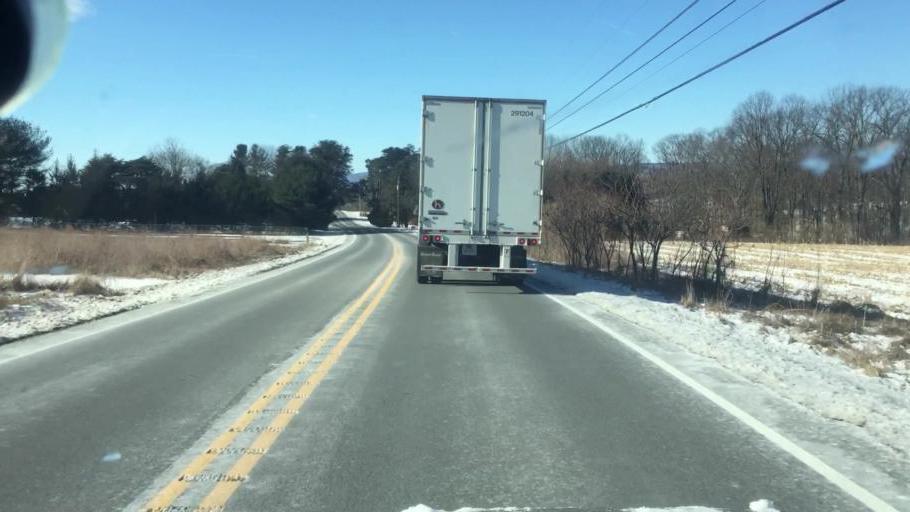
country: US
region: Pennsylvania
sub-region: Luzerne County
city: Nescopeck
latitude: 41.0501
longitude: -76.1553
